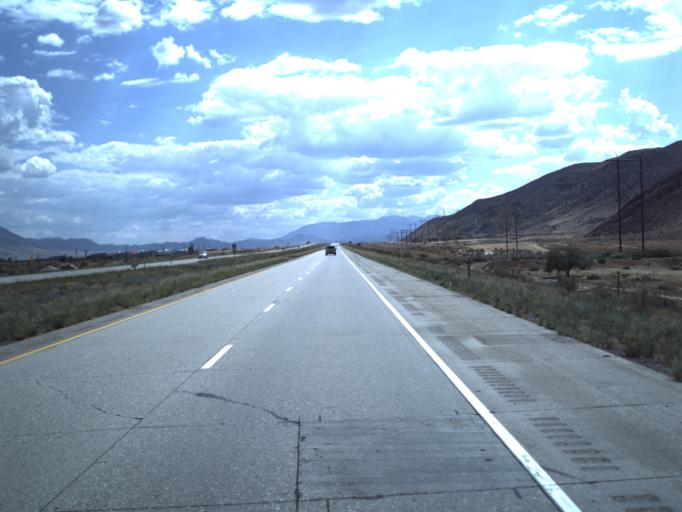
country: US
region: Utah
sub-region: Sevier County
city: Richfield
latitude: 38.7238
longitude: -112.1307
